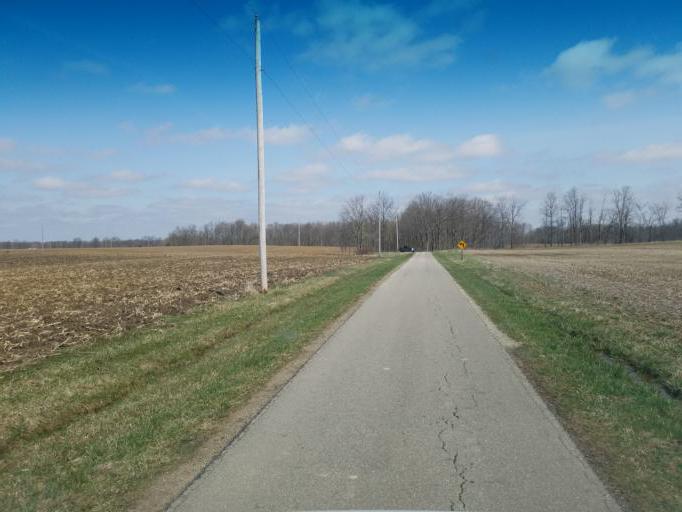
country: US
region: Ohio
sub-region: Crawford County
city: Bucyrus
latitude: 40.9271
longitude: -83.0597
